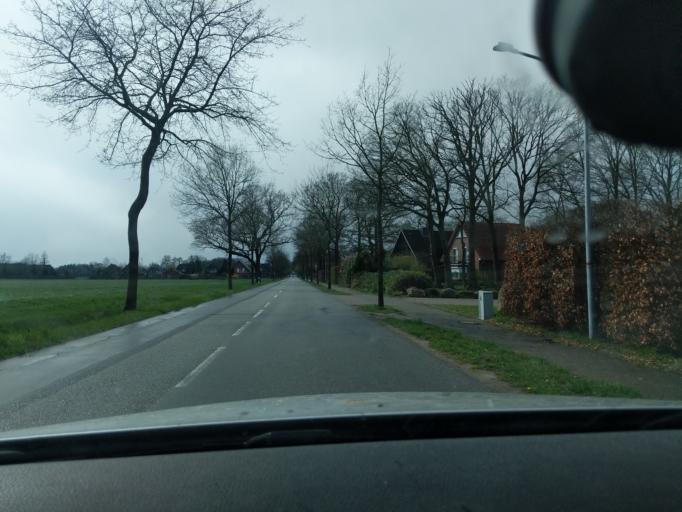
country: DE
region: Lower Saxony
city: Ahlerstedt
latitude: 53.4022
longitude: 9.4635
